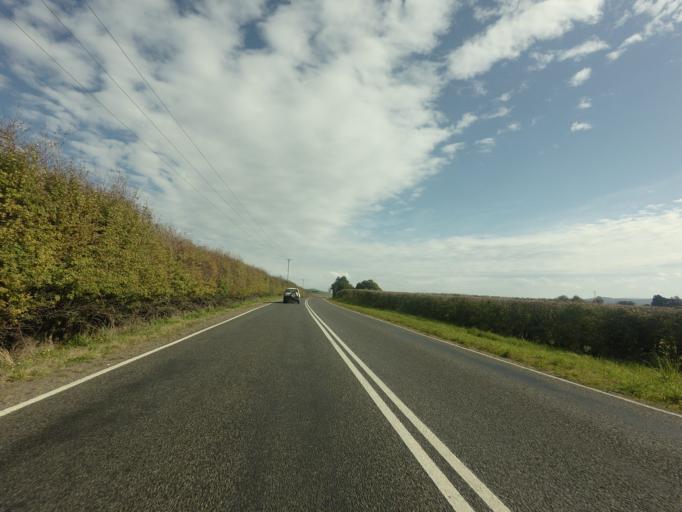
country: AU
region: Tasmania
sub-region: Meander Valley
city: Westbury
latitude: -41.5235
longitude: 146.7736
